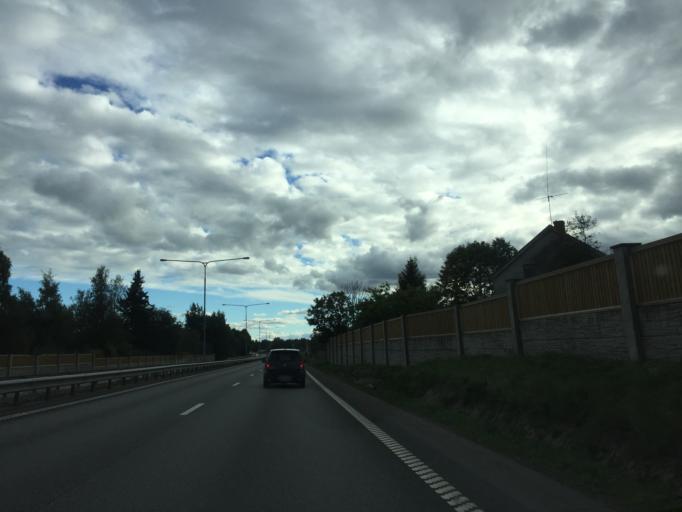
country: SE
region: OErebro
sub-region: Orebro Kommun
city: Hovsta
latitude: 59.3150
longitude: 15.2292
